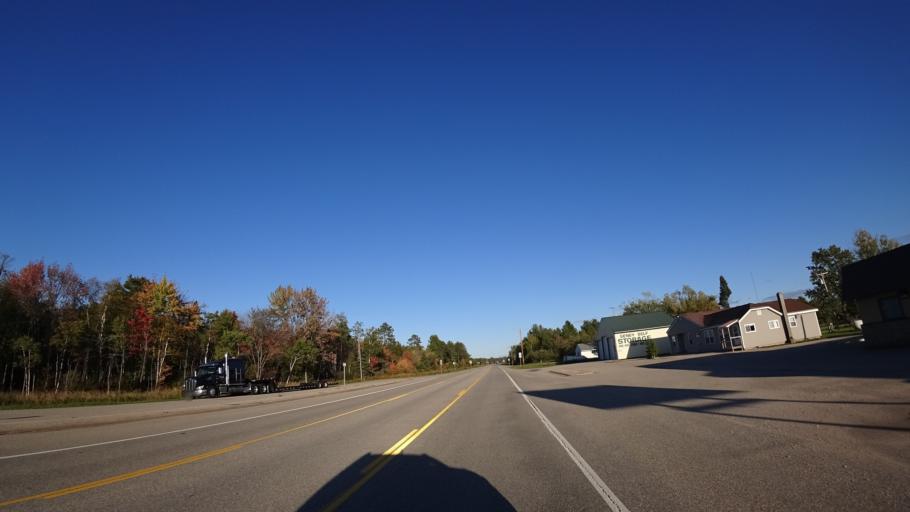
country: US
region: Michigan
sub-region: Luce County
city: Newberry
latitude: 46.3456
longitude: -85.9447
